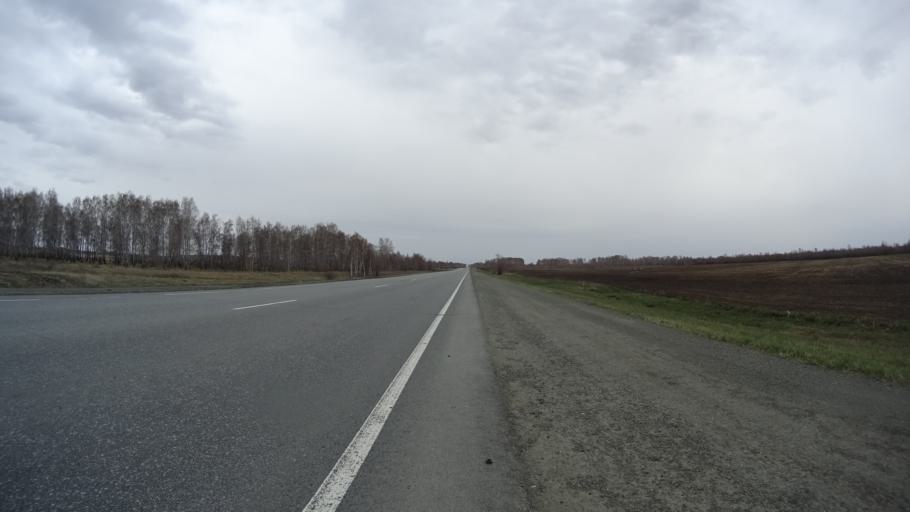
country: RU
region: Chelyabinsk
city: Krasnogorskiy
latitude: 54.6604
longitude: 61.2551
